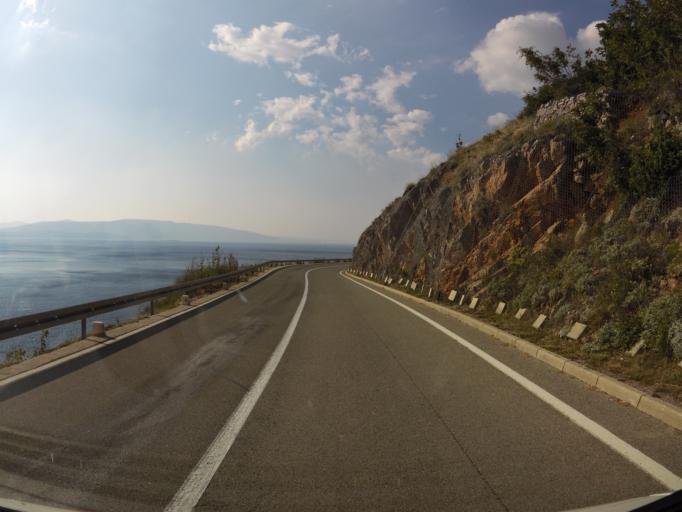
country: HR
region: Licko-Senjska
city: Senj
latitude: 44.9775
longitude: 14.9148
